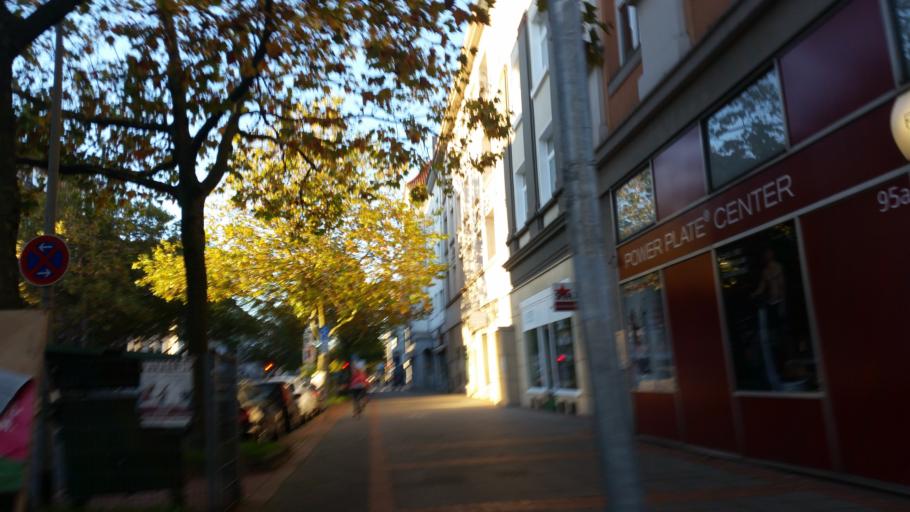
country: DE
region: Lower Saxony
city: Hannover
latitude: 52.3586
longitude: 9.7519
